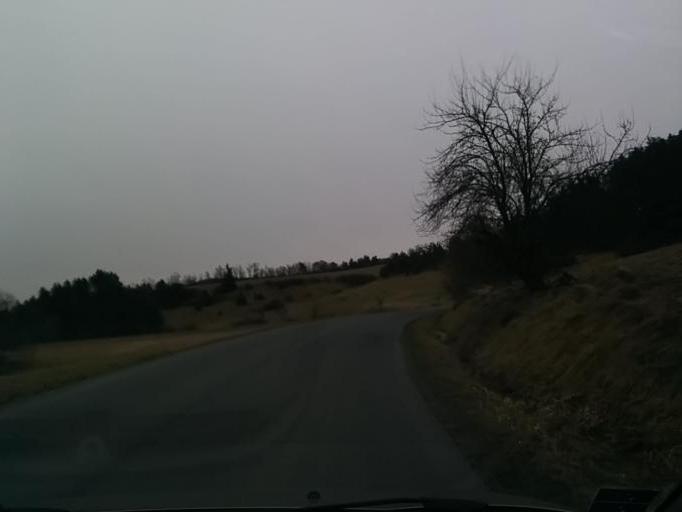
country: SK
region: Banskobystricky
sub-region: Okres Banska Bystrica
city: Zvolen
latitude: 48.6381
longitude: 19.1905
